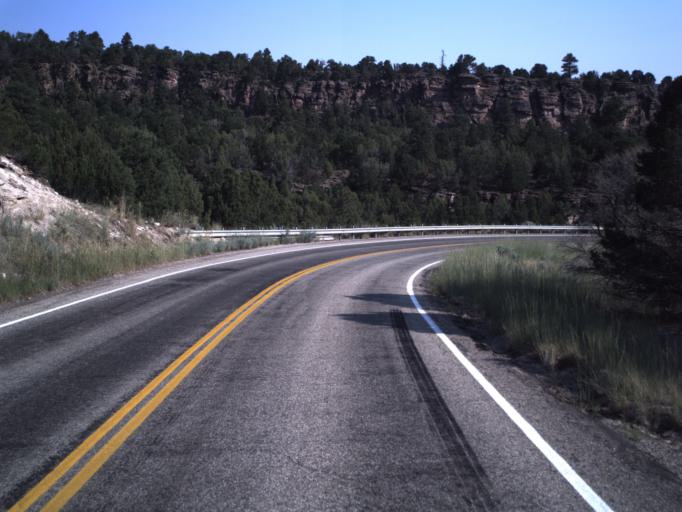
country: US
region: Utah
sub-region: Daggett County
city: Manila
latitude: 40.8969
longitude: -109.4470
